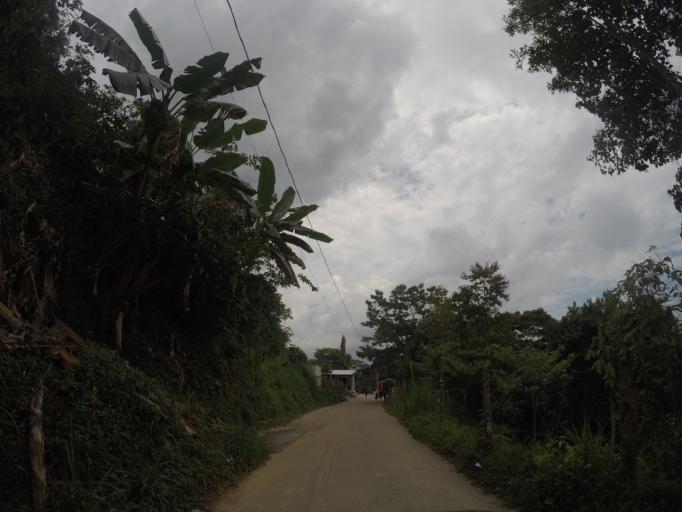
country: MX
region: Oaxaca
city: Pluma Hidalgo
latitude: 15.9210
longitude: -96.4166
